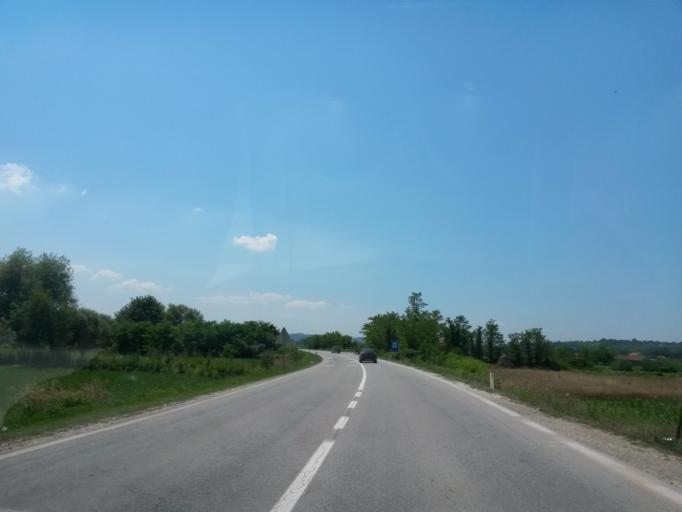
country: BA
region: Republika Srpska
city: Doboj
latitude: 44.8016
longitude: 18.0471
